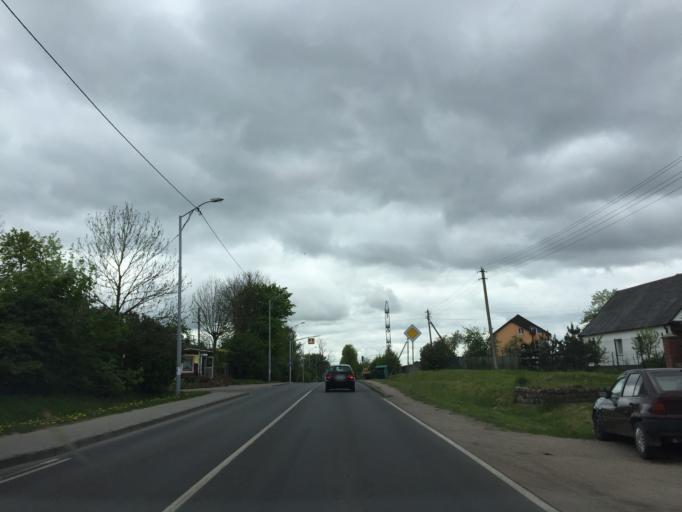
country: RU
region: Kaliningrad
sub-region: Gorod Kaliningrad
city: Kaliningrad
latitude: 54.6724
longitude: 20.4352
